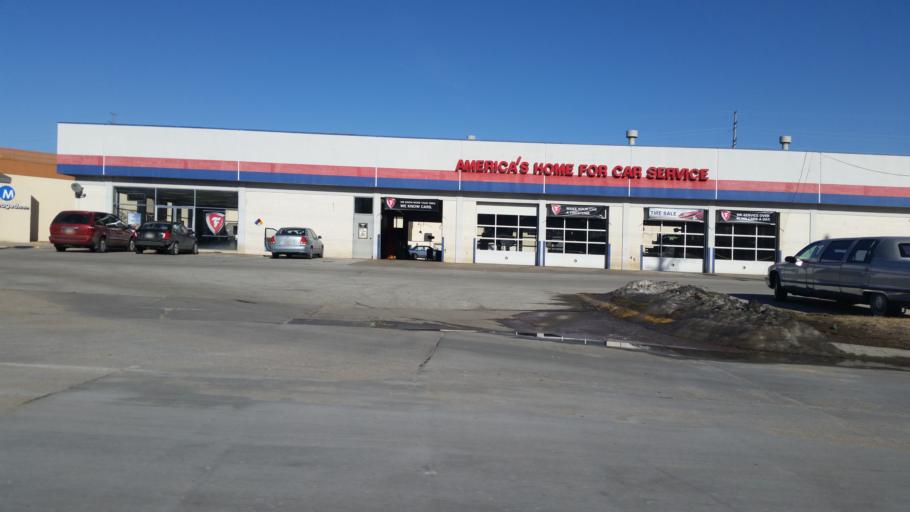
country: US
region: Nebraska
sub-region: Sarpy County
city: Bellevue
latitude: 41.1769
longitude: -95.9265
